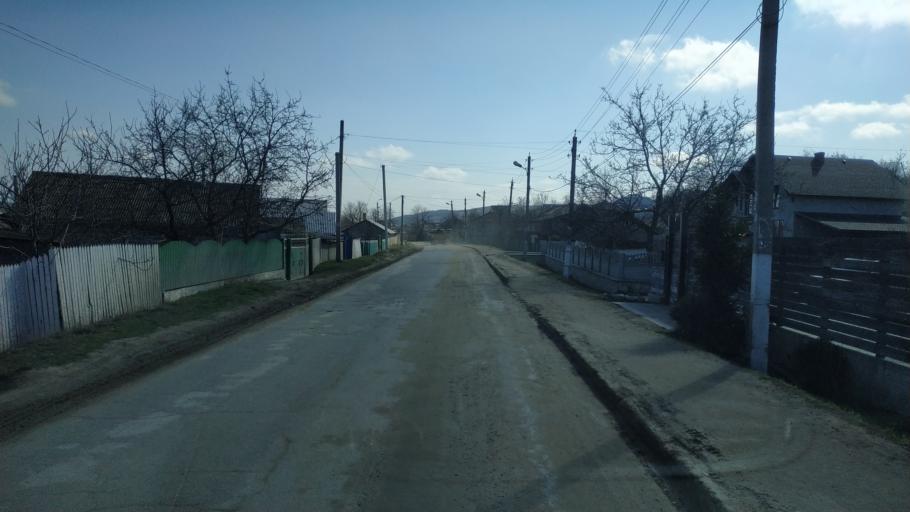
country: MD
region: Hincesti
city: Hincesti
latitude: 46.9338
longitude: 28.6442
